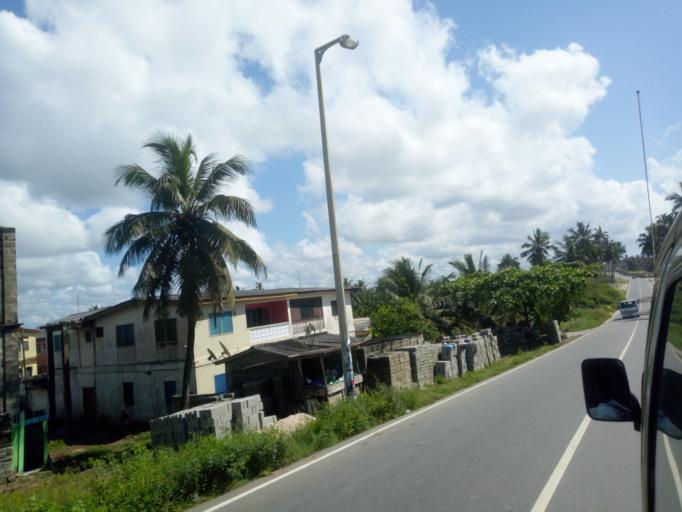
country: GH
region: Central
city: Elmina
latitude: 5.0917
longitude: -1.3435
